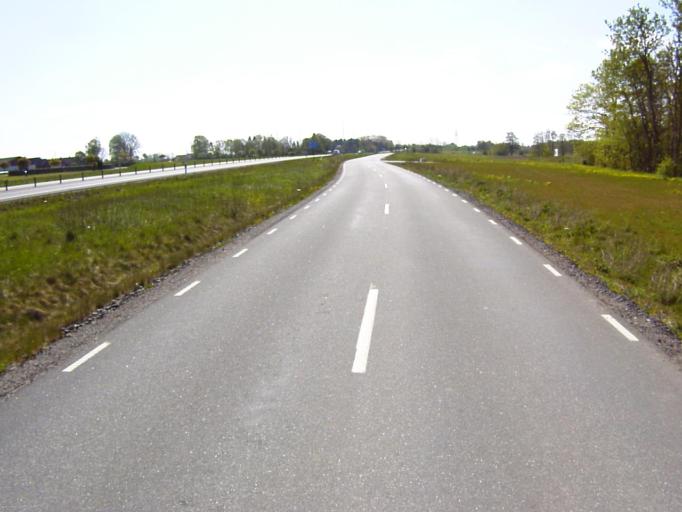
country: SE
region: Skane
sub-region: Kristianstads Kommun
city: Fjalkinge
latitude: 56.0048
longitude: 14.2635
